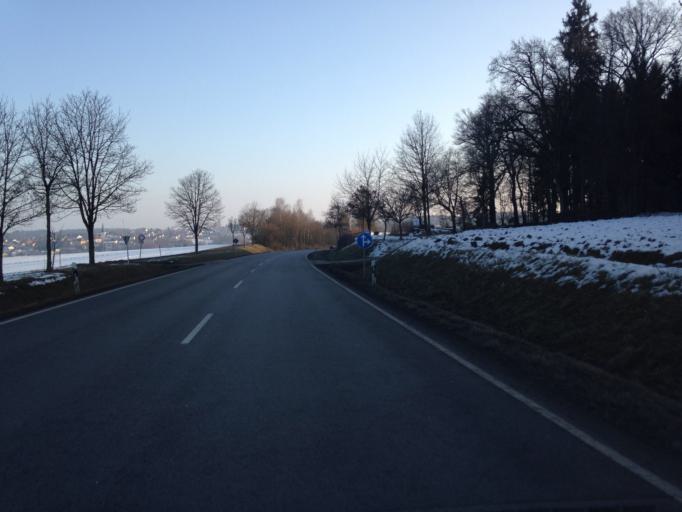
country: DE
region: Bavaria
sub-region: Lower Bavaria
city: Simbach
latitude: 48.5752
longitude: 12.7262
